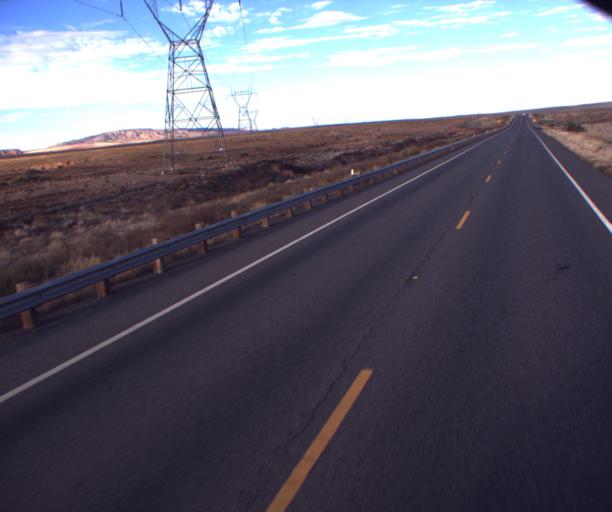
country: US
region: Arizona
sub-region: Apache County
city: Lukachukai
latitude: 36.9368
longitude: -109.2391
